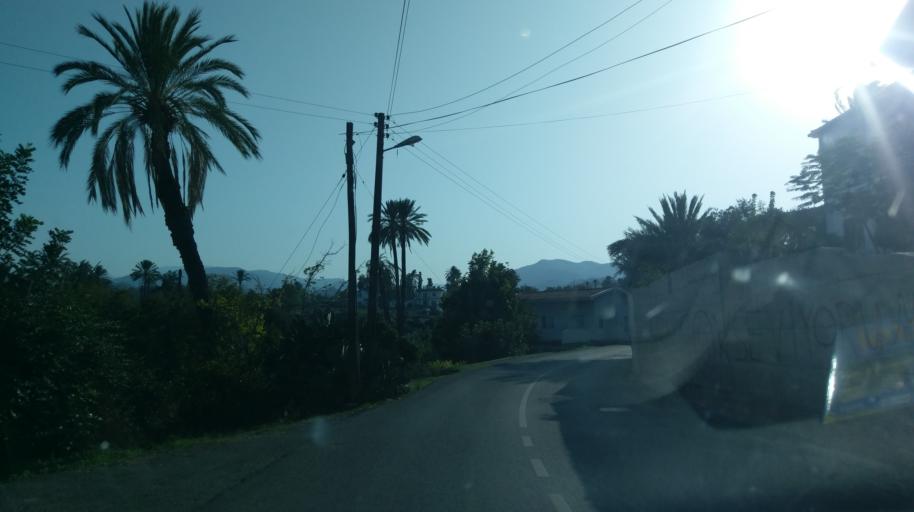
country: CY
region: Lefkosia
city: Lefka
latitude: 35.1041
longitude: 32.8493
